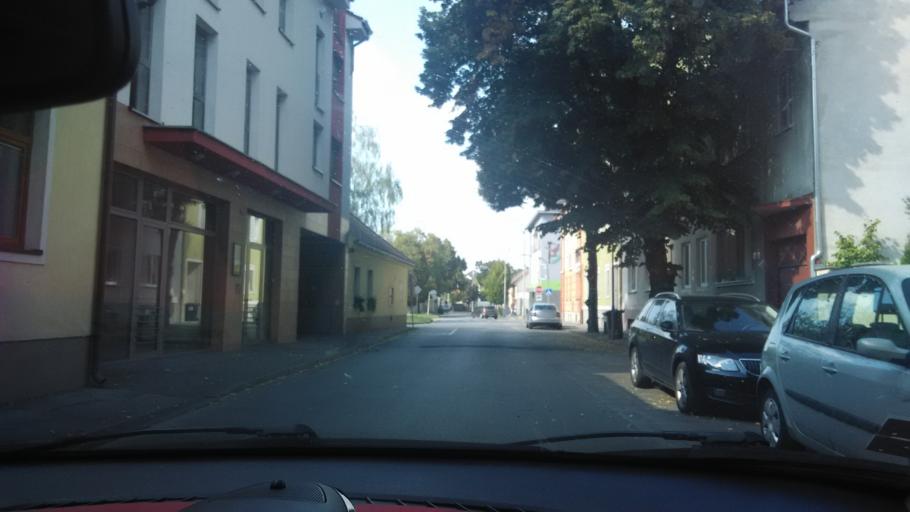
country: SK
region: Trnavsky
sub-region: Okres Trnava
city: Piestany
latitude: 48.5946
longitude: 17.8329
